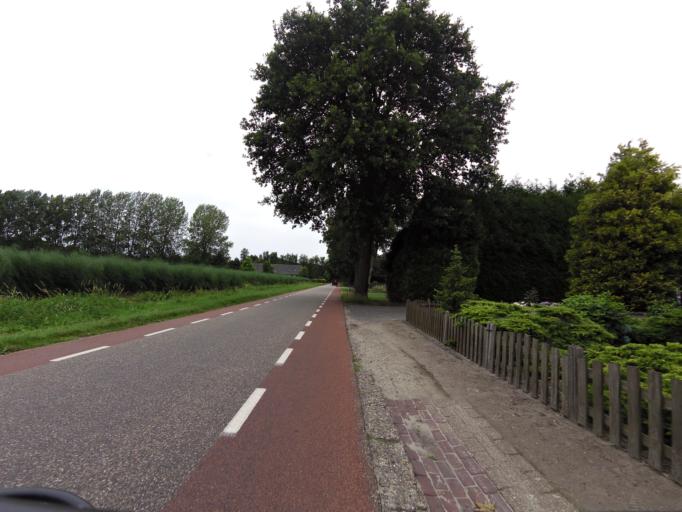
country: NL
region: North Brabant
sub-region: Gemeente Son en Breugel
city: Breugel
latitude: 51.5341
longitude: 5.5086
